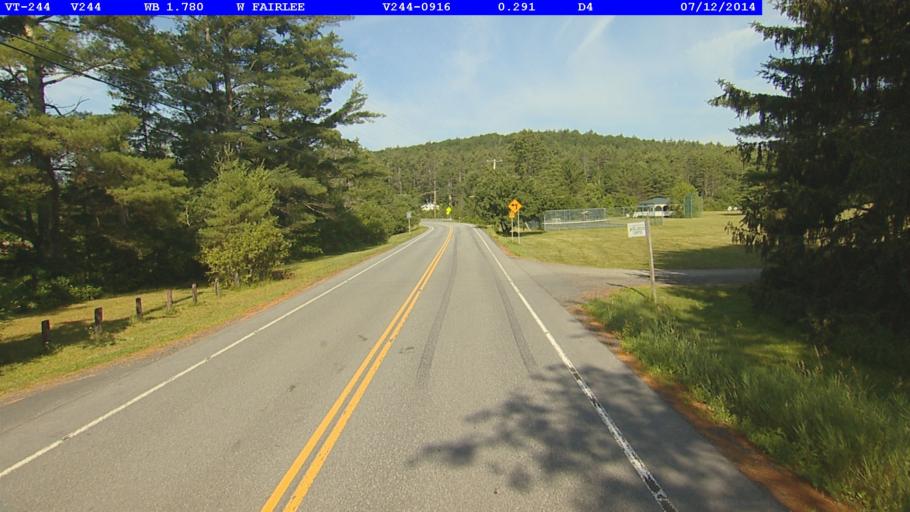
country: US
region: New Hampshire
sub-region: Grafton County
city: Orford
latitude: 43.8908
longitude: -72.2282
